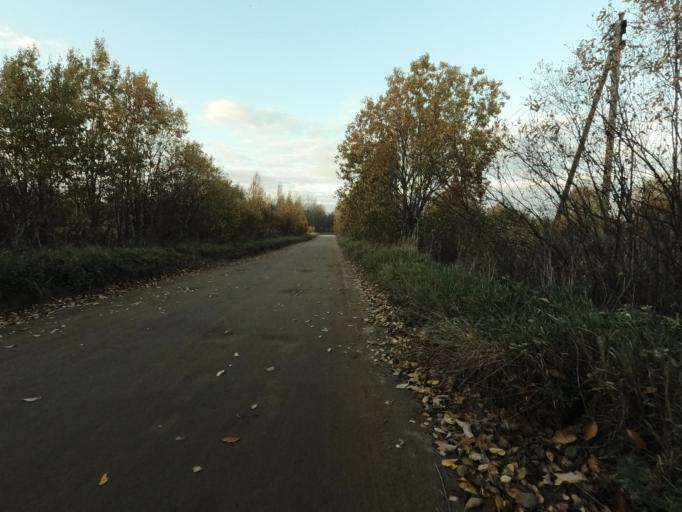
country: RU
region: Leningrad
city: Mga
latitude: 59.8050
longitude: 31.2009
